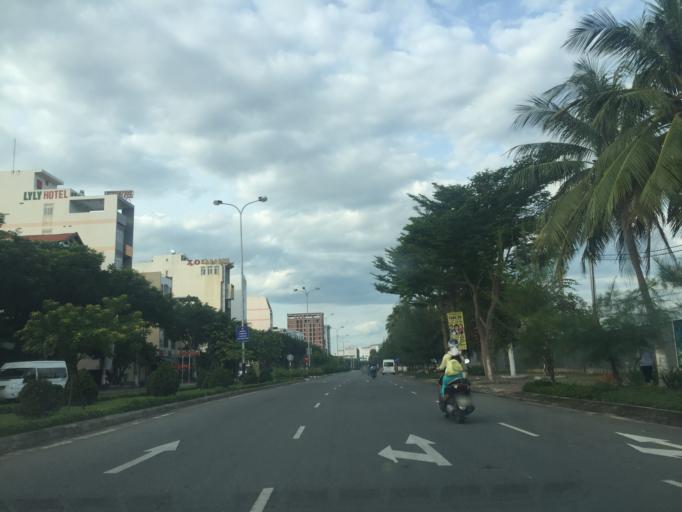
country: VN
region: Da Nang
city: Da Nang
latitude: 16.0824
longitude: 108.2125
